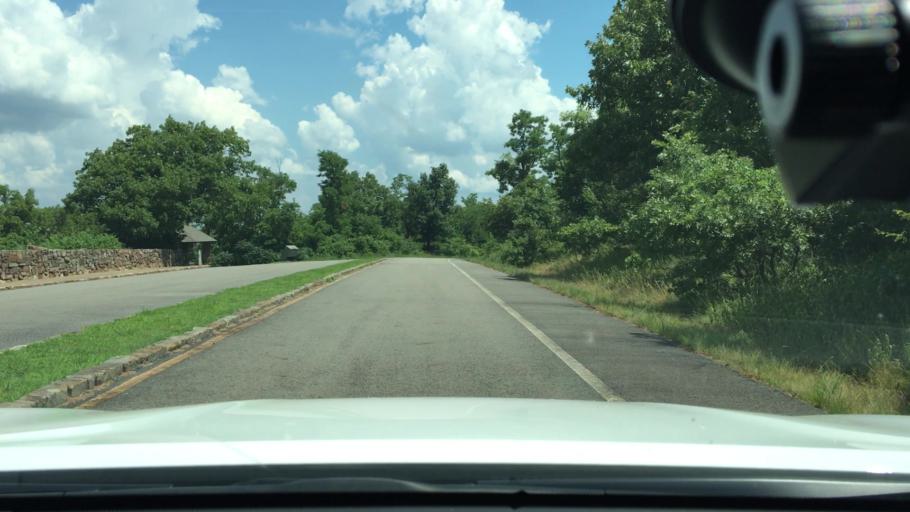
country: US
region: Arkansas
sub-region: Logan County
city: Paris
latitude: 35.1754
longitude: -93.6460
